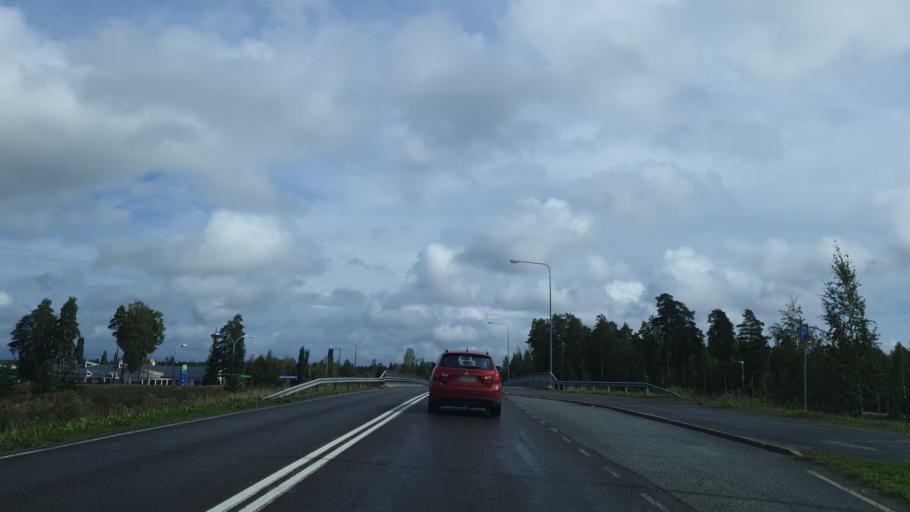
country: FI
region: Northern Savo
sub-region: Varkaus
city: Varkaus
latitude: 62.3310
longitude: 27.8225
